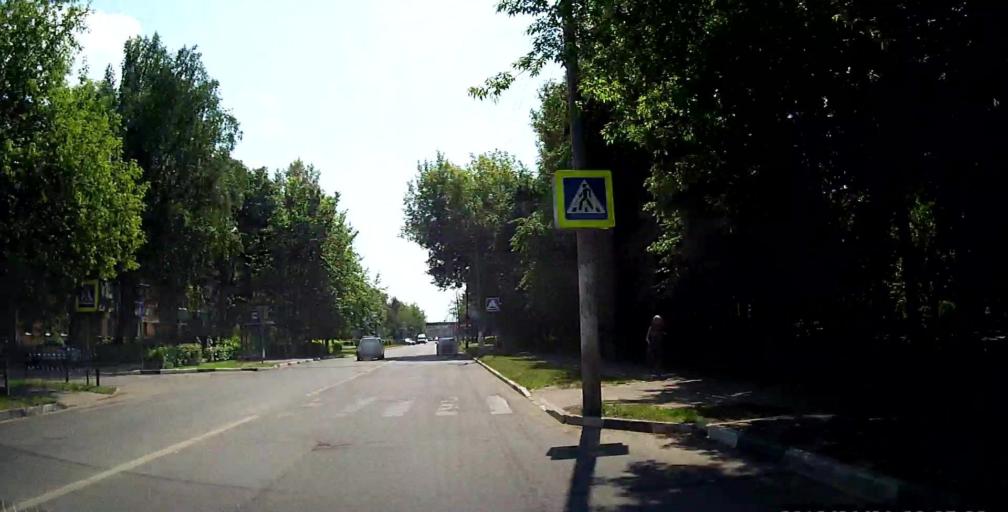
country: RU
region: Moskovskaya
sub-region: Podol'skiy Rayon
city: Podol'sk
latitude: 55.4172
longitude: 37.5318
